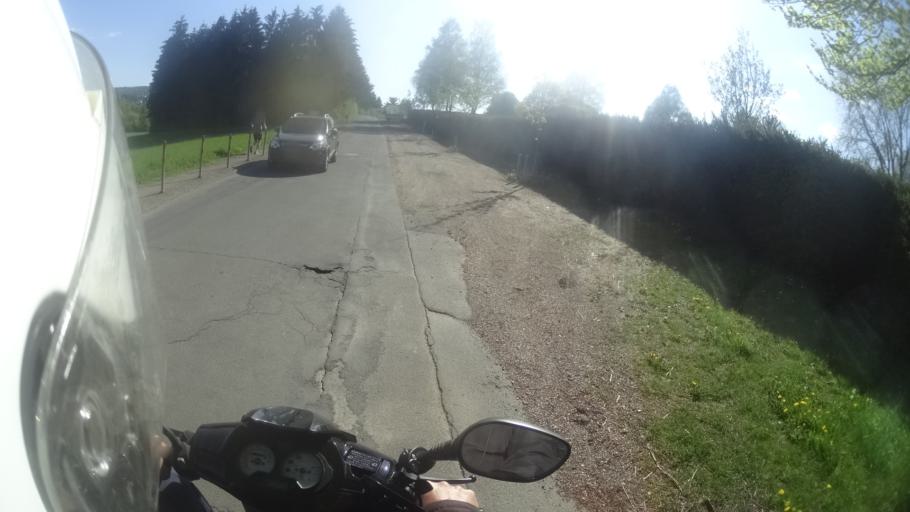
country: DE
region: Hesse
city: Taunusstein
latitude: 50.1444
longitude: 8.1470
